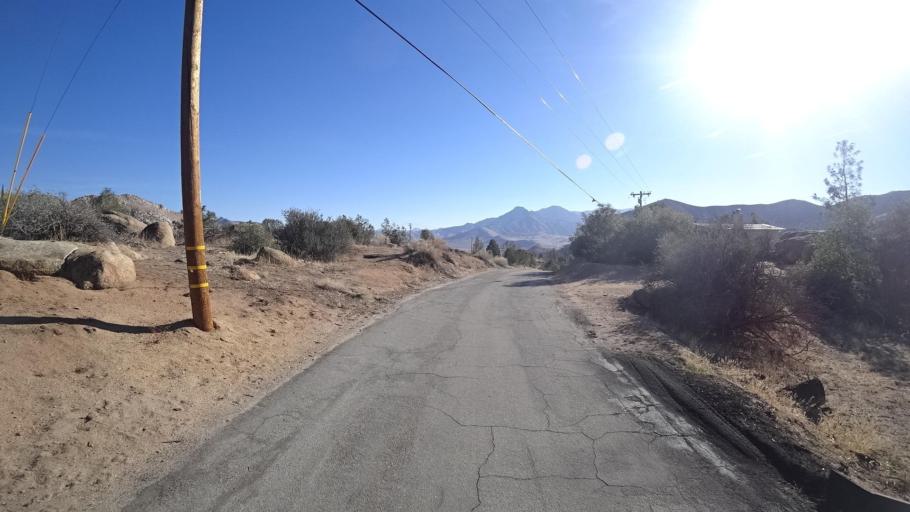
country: US
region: California
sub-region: Kern County
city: Weldon
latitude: 35.7131
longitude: -118.3050
